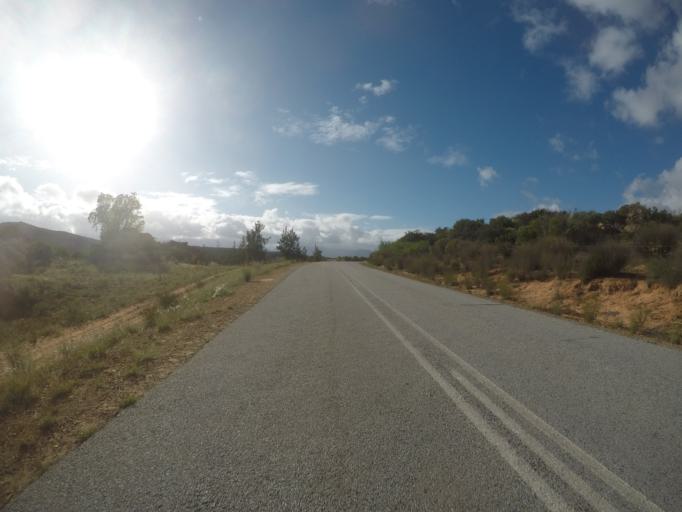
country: ZA
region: Western Cape
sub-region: West Coast District Municipality
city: Clanwilliam
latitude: -32.4255
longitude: 18.9353
